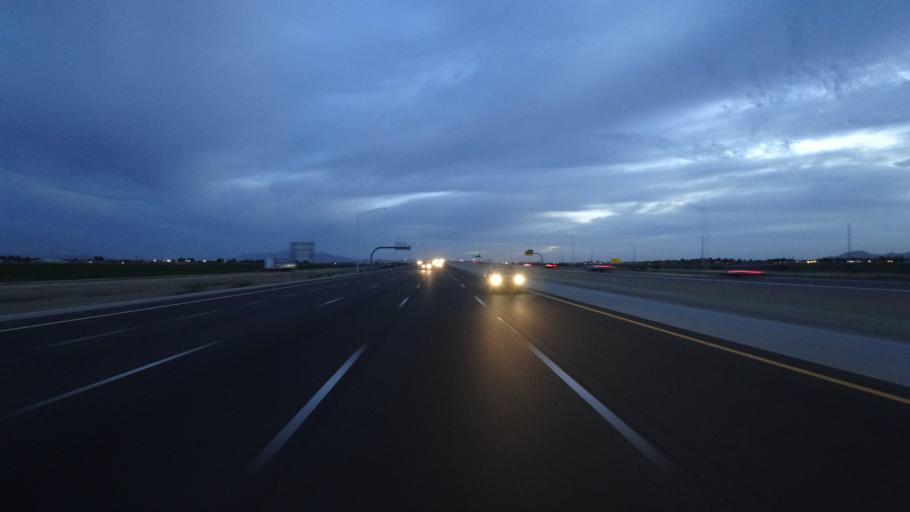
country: US
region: Arizona
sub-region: Maricopa County
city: Citrus Park
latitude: 33.5434
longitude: -112.4181
